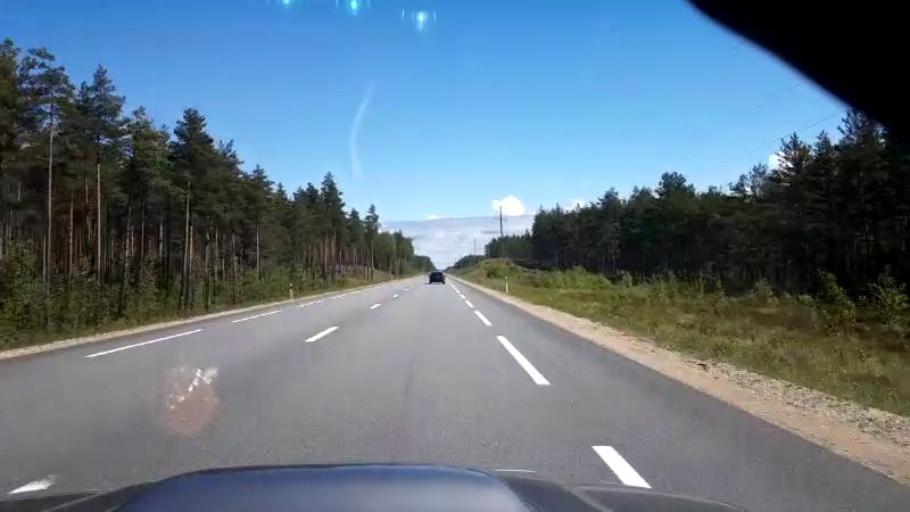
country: LV
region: Saulkrastu
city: Saulkrasti
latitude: 57.2042
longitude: 24.3808
